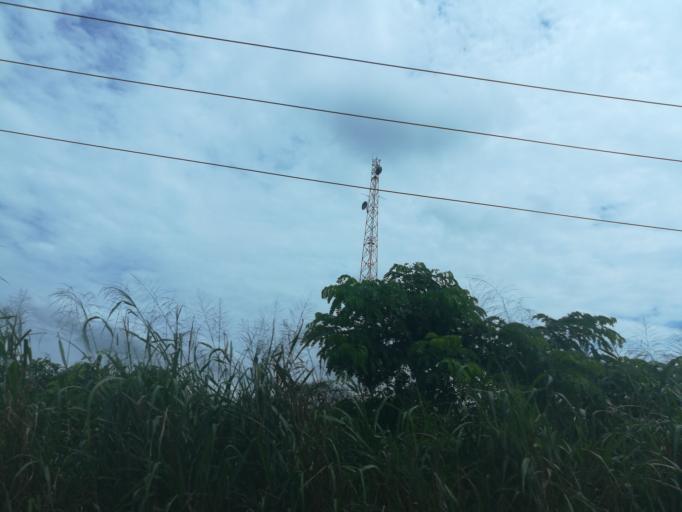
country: NG
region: Lagos
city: Ikotun
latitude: 6.4937
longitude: 3.1511
